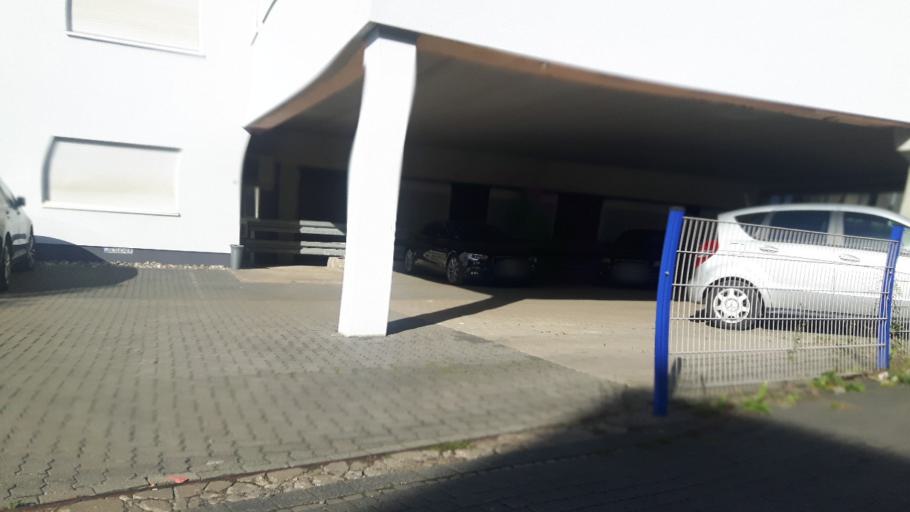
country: DE
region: North Rhine-Westphalia
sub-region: Regierungsbezirk Arnsberg
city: Siegen
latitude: 50.9058
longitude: 8.0381
